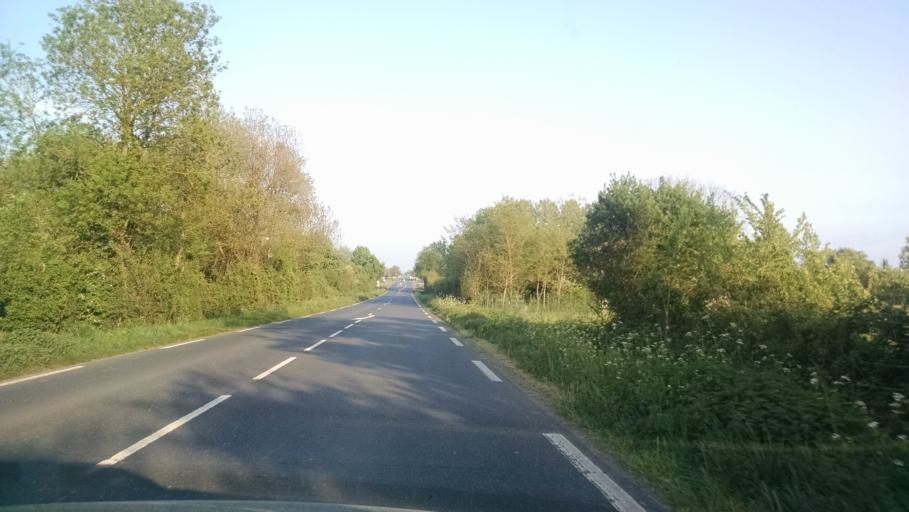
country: FR
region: Pays de la Loire
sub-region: Departement de la Loire-Atlantique
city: Boussay
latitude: 47.0617
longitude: -1.1904
